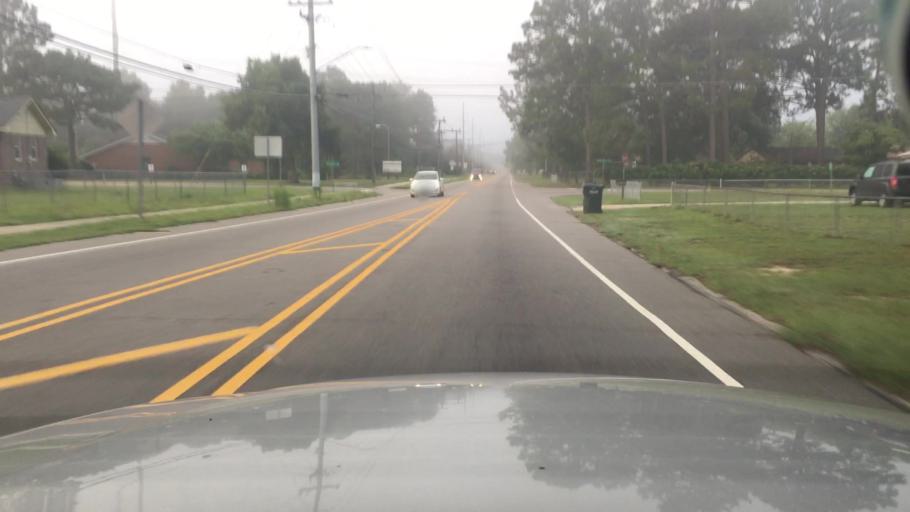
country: US
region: North Carolina
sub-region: Cumberland County
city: Hope Mills
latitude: 35.0212
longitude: -78.9402
